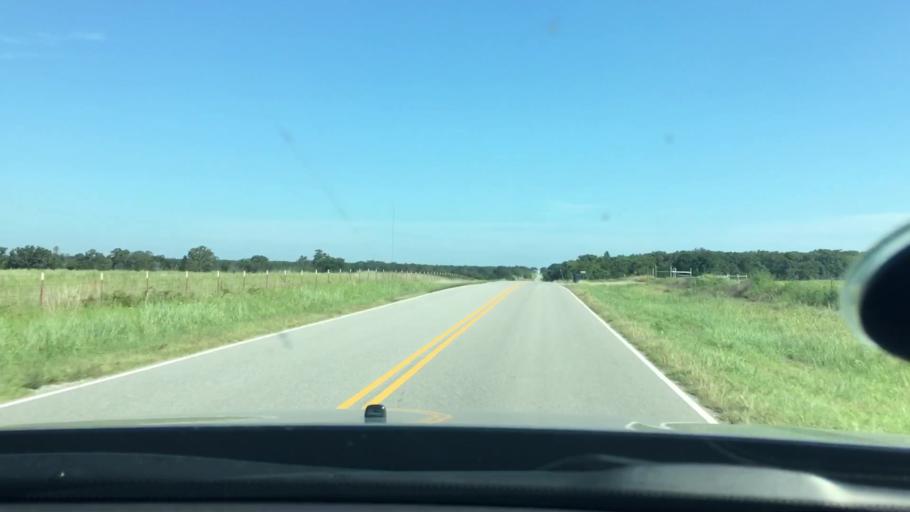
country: US
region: Oklahoma
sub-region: Johnston County
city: Tishomingo
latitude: 34.3064
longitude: -96.5488
